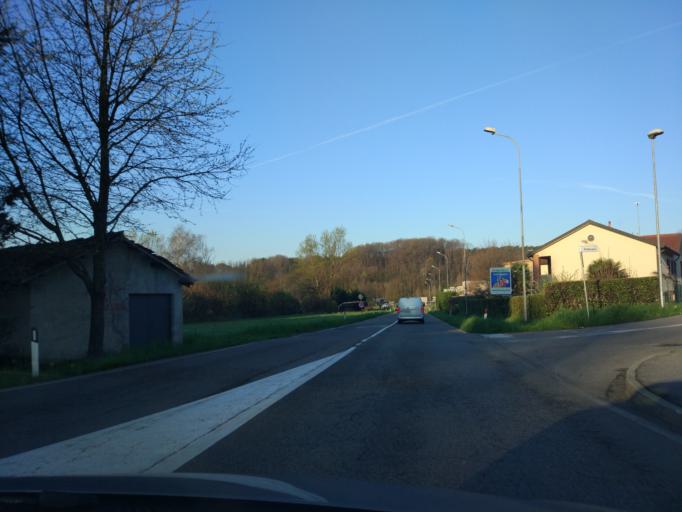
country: IT
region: Lombardy
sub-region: Provincia di Como
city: Alzate Brianza
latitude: 45.7675
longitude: 9.1793
